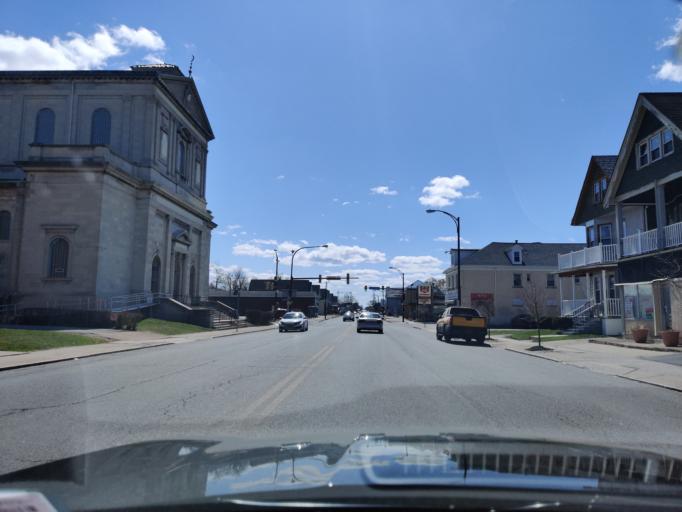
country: US
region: New York
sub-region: Erie County
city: Sloan
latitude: 42.9231
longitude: -78.8131
